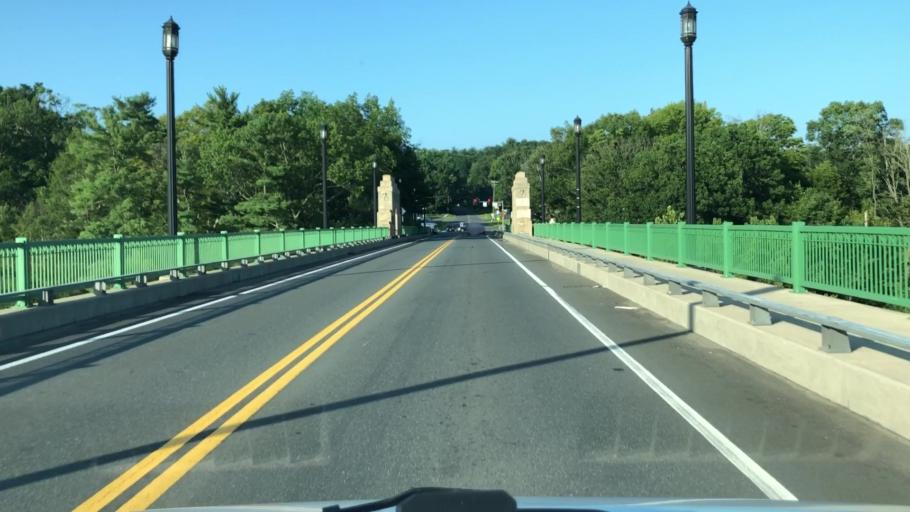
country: US
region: Massachusetts
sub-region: Franklin County
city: Turners Falls
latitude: 42.6121
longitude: -72.5506
